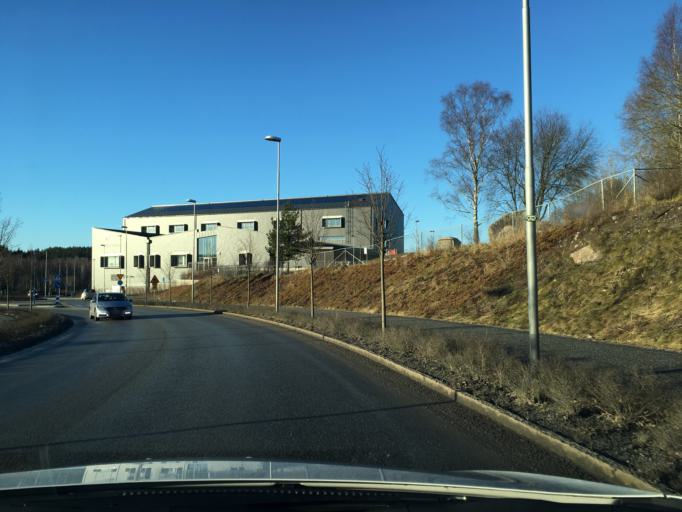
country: SE
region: Uppsala
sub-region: Knivsta Kommun
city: Knivsta
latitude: 59.7308
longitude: 17.7885
